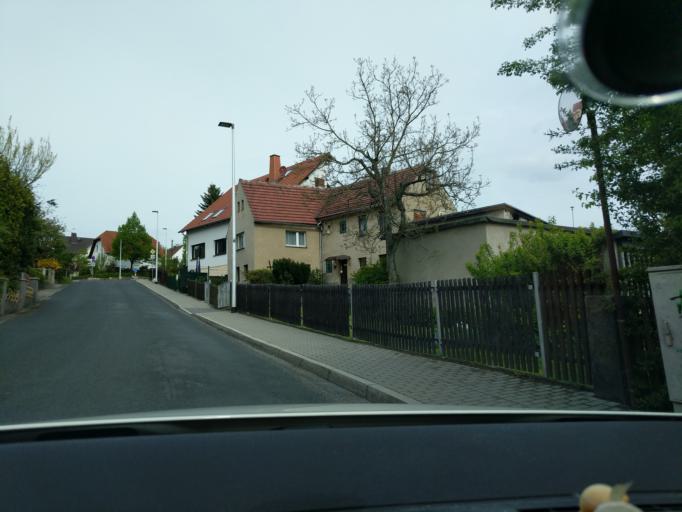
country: DE
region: Saxony
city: Bannewitz
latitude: 50.9971
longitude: 13.6887
